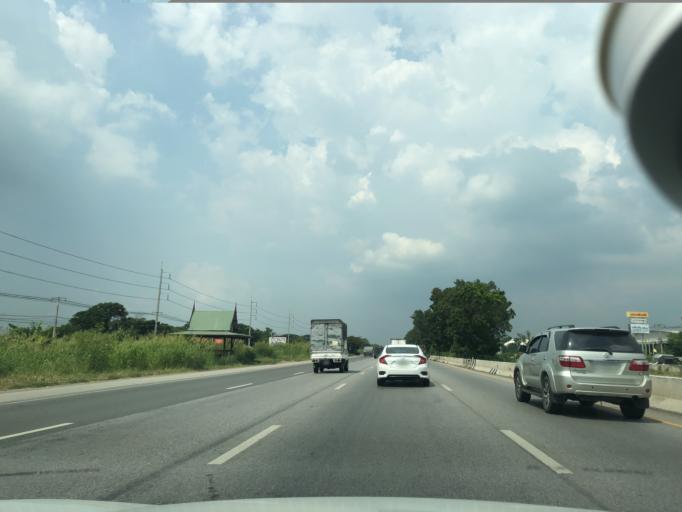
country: TH
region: Phra Nakhon Si Ayutthaya
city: Maha Rat
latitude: 14.5348
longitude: 100.5038
